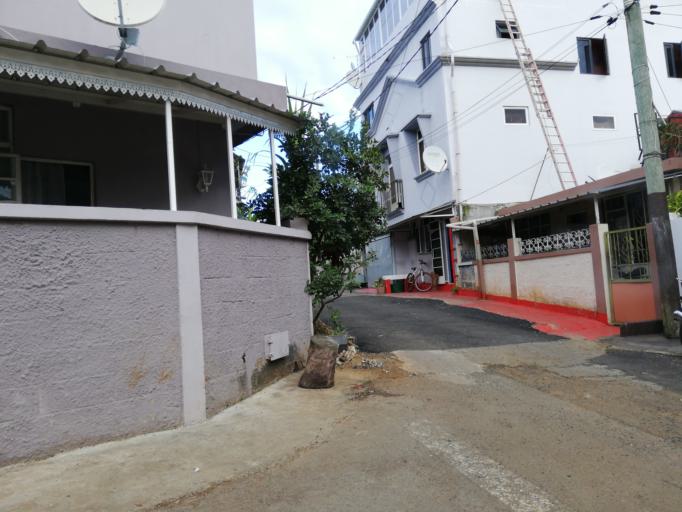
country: MU
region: Black River
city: Petite Riviere
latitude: -20.2226
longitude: 57.4616
